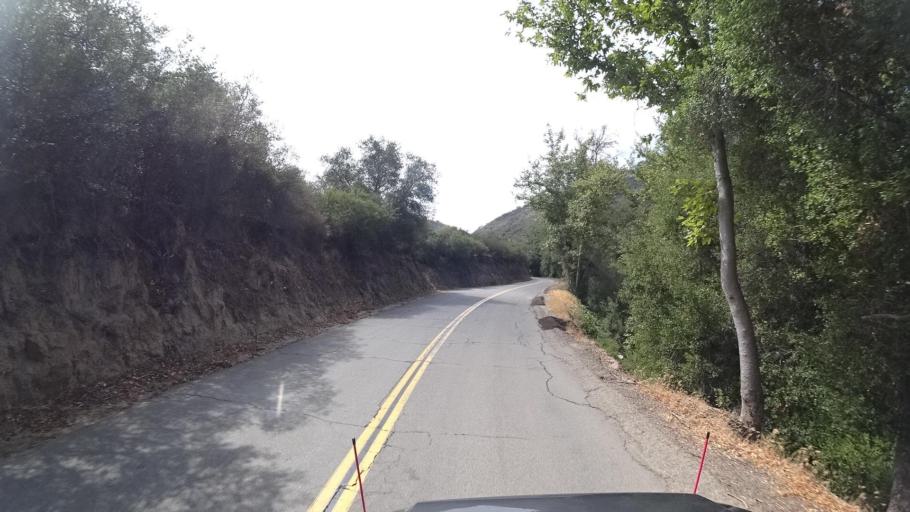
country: US
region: California
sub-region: San Diego County
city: Fallbrook
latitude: 33.4245
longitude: -117.2488
